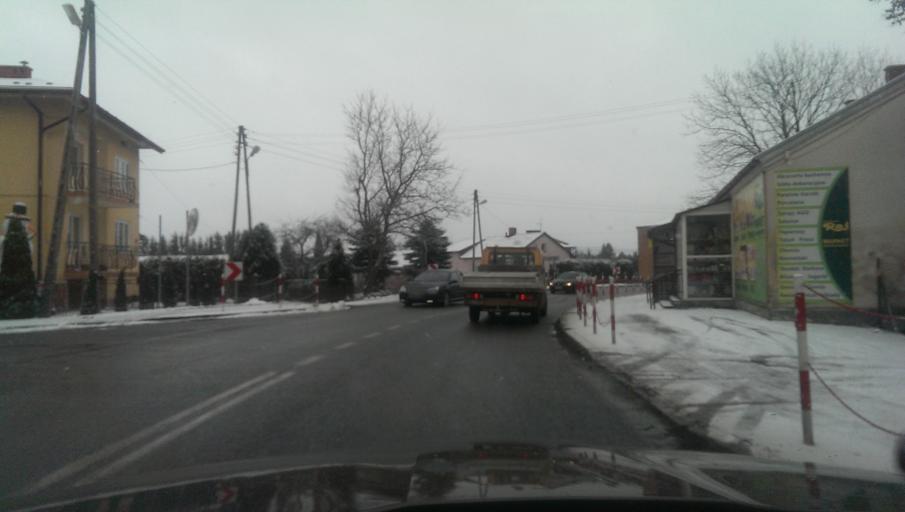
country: PL
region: Subcarpathian Voivodeship
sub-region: Powiat sanocki
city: Zarszyn
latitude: 49.5836
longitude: 22.0155
